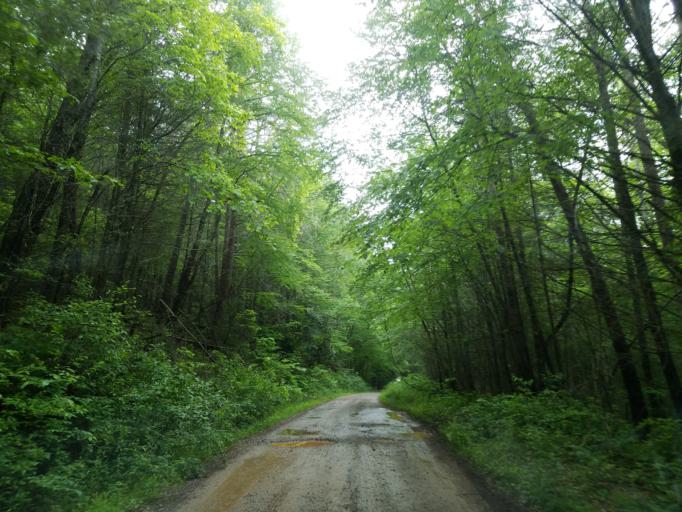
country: US
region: Georgia
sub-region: Union County
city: Blairsville
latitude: 34.7562
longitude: -84.0040
